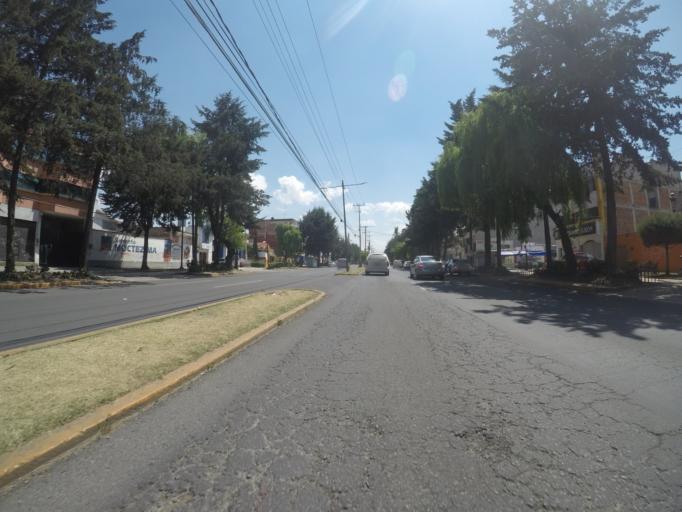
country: MX
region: Mexico
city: San Buenaventura
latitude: 19.2599
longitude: -99.6625
